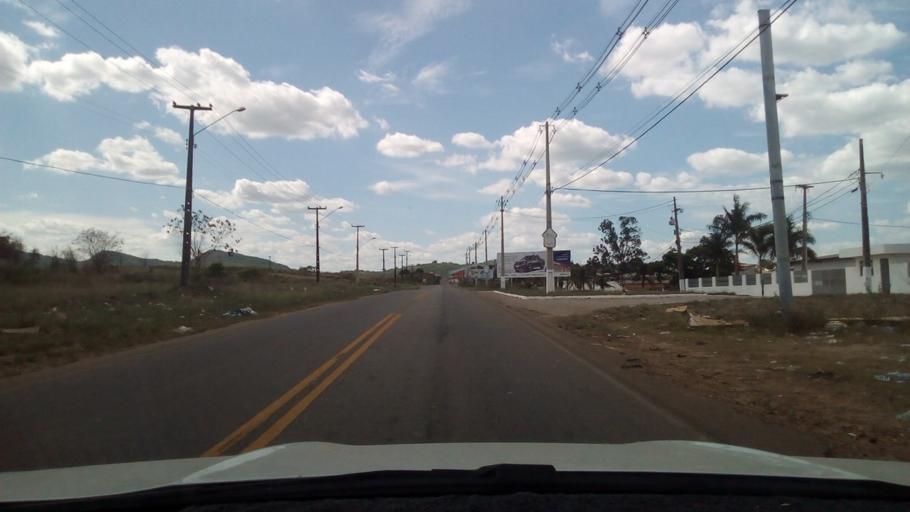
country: BR
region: Paraiba
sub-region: Guarabira
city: Guarabira
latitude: -6.8738
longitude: -35.4823
